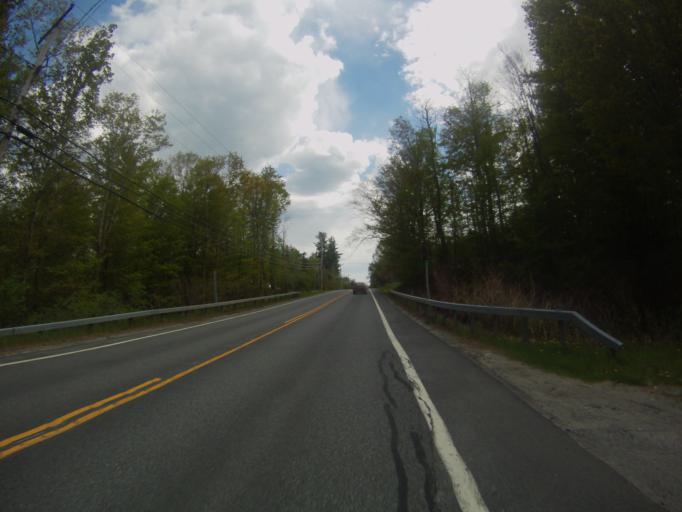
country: US
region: New York
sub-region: Essex County
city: Ticonderoga
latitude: 43.8591
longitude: -73.7557
